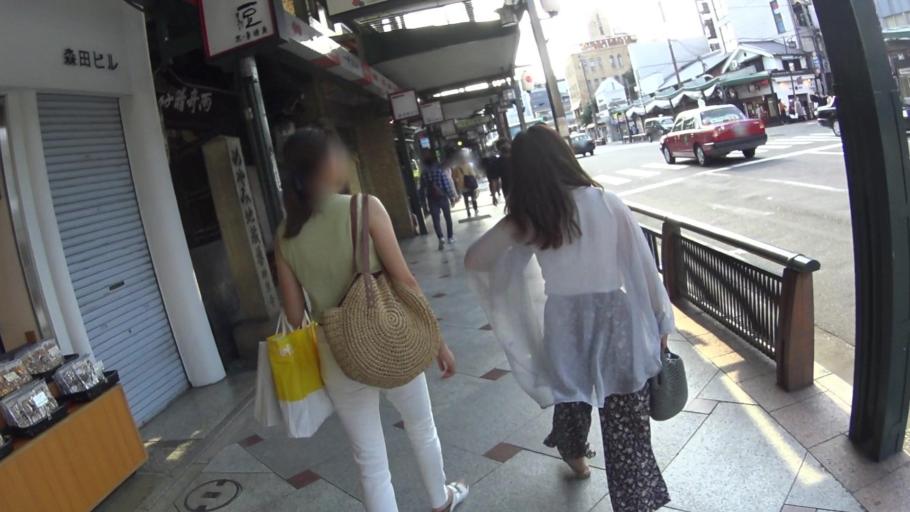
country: RU
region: Rostov
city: Remontnoye
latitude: 46.5030
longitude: 43.7454
